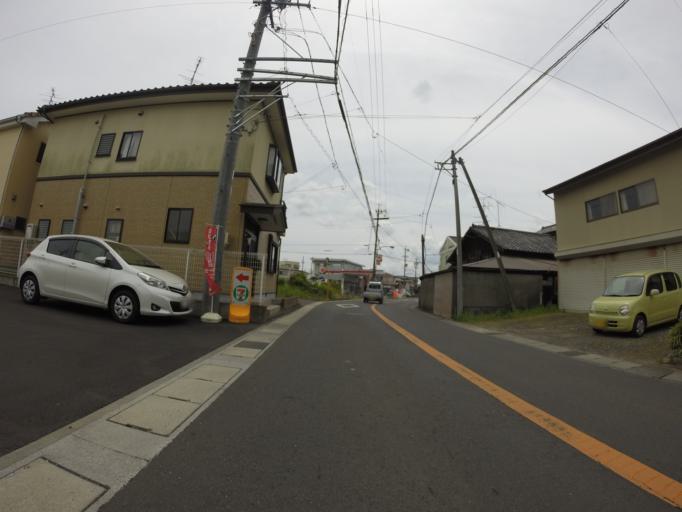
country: JP
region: Shizuoka
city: Shizuoka-shi
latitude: 35.0136
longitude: 138.4135
